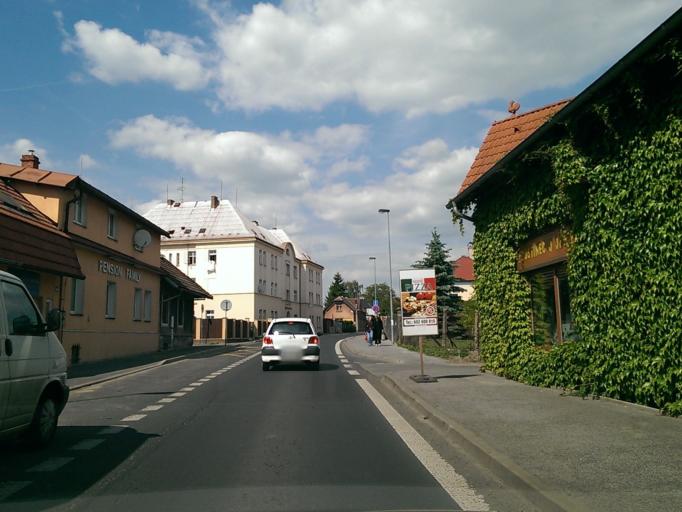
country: CZ
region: Central Bohemia
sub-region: Okres Melnik
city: Melnik
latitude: 50.3407
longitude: 14.4928
